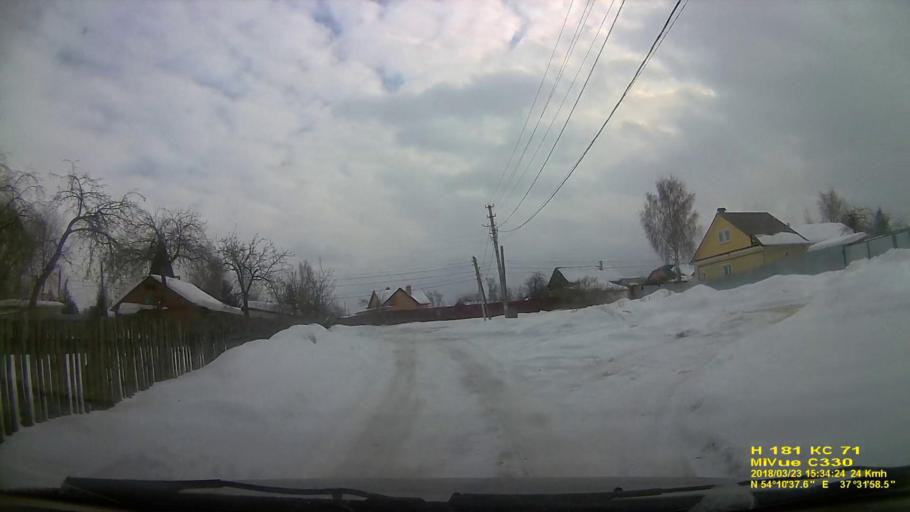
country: RU
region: Tula
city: Kosaya Gora
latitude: 54.1771
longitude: 37.5329
